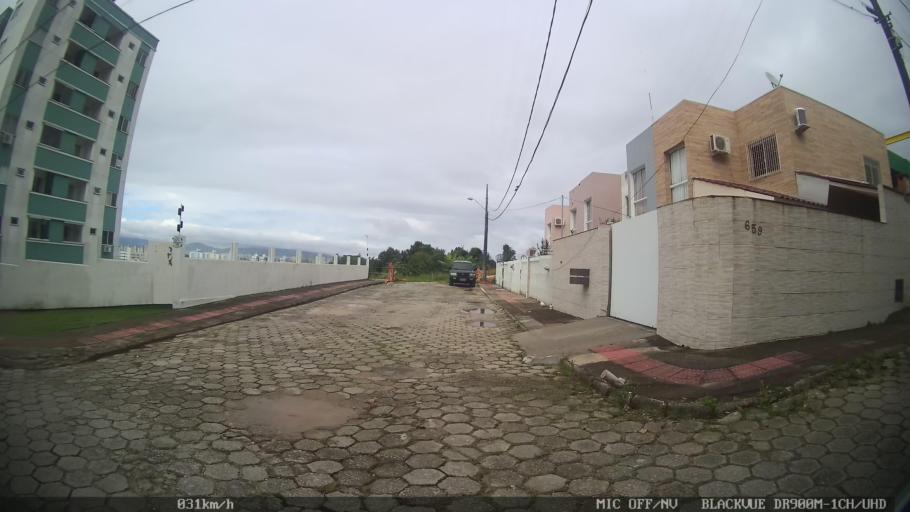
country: BR
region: Santa Catarina
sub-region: Sao Jose
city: Campinas
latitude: -27.5544
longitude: -48.6398
